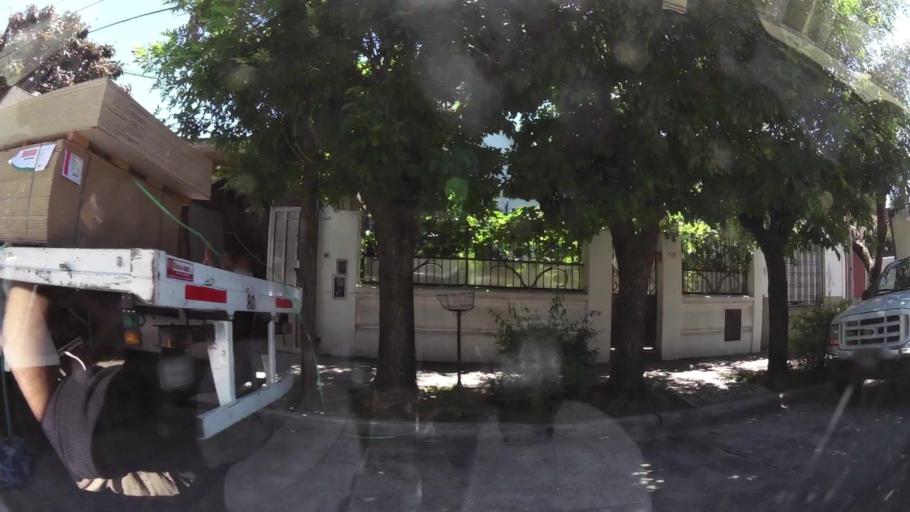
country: AR
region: Buenos Aires
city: Caseros
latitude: -34.5978
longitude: -58.5376
